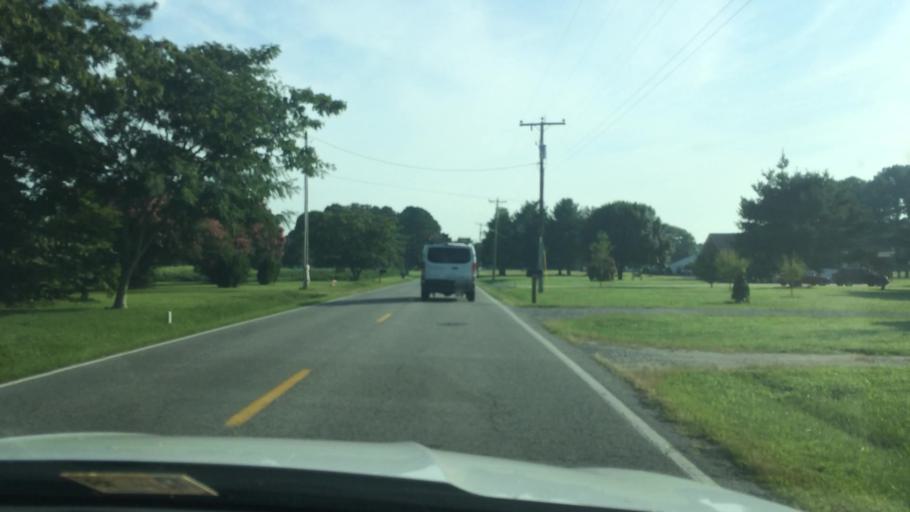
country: US
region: Virginia
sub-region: Gloucester County
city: Gloucester Courthouse
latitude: 37.4867
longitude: -76.4409
